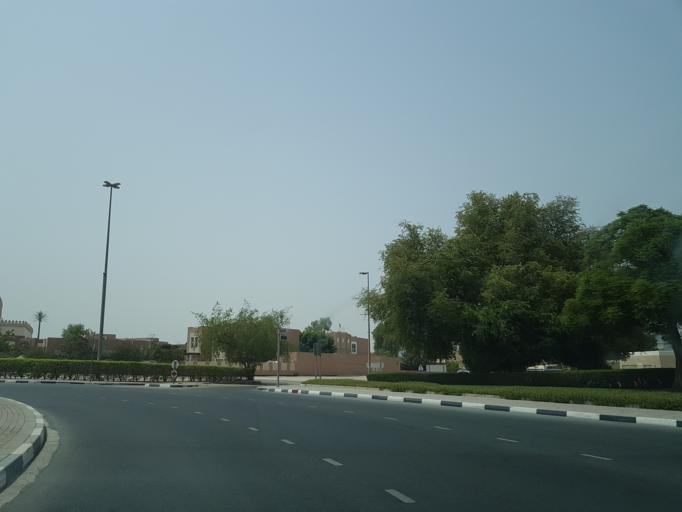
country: AE
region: Ash Shariqah
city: Sharjah
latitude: 25.2261
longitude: 55.2983
